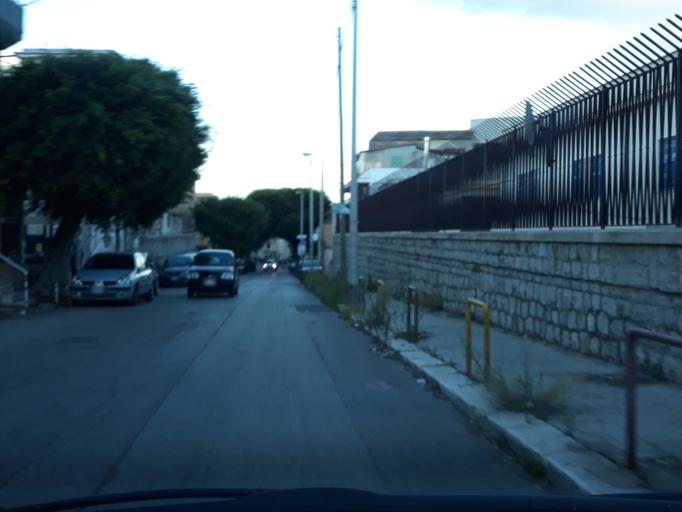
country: IT
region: Sicily
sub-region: Palermo
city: Villa Ciambra
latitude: 38.0907
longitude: 13.3317
